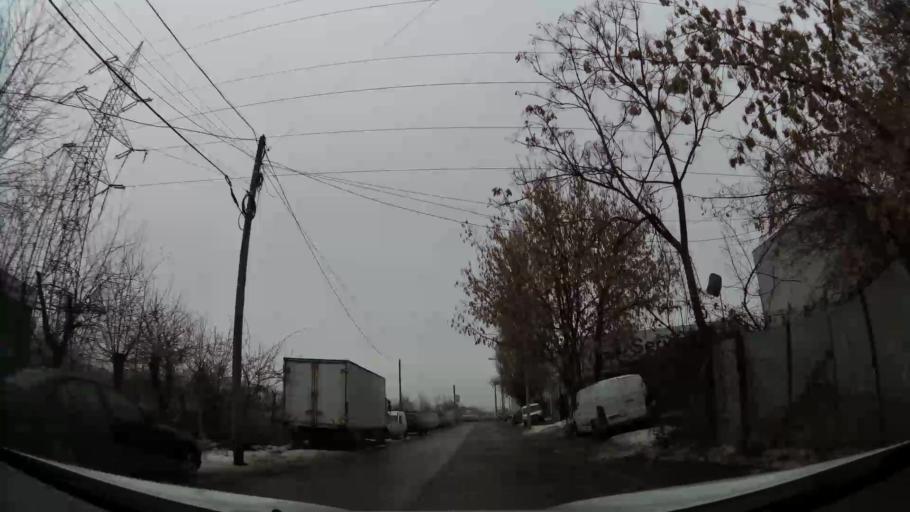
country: RO
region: Ilfov
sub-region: Comuna Popesti-Leordeni
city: Popesti-Leordeni
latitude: 44.4030
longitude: 26.1495
